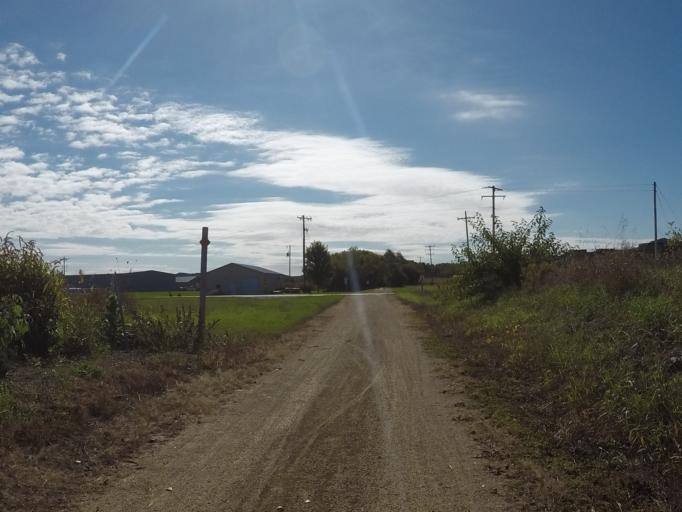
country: US
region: Wisconsin
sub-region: Richland County
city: Richland Center
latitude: 43.2933
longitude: -90.3281
